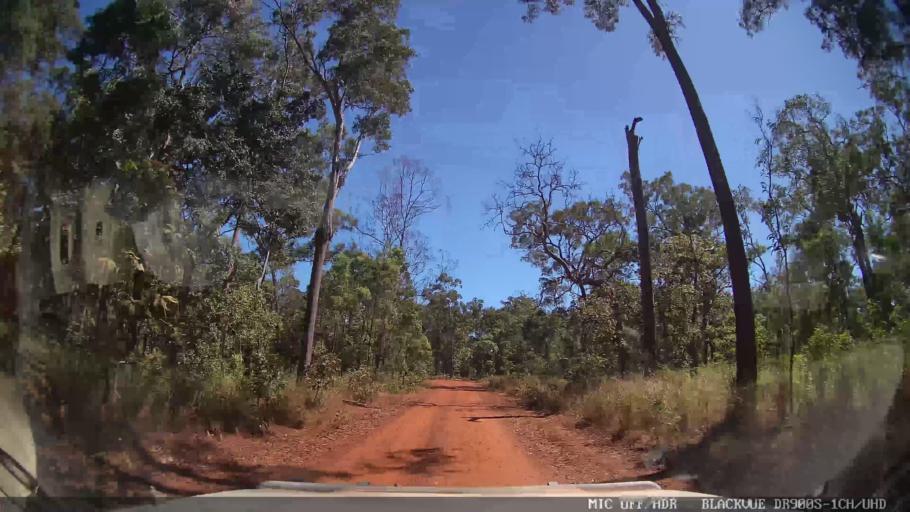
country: AU
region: Queensland
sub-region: Torres
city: Thursday Island
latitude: -10.9157
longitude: 142.2546
